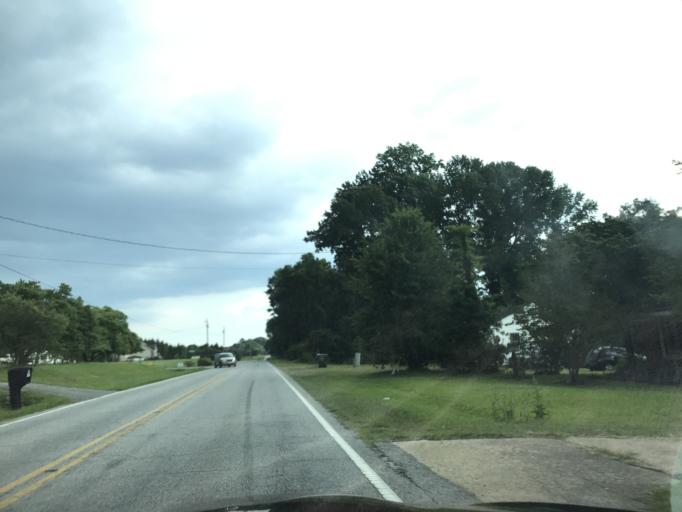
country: US
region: North Carolina
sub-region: Johnston County
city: Four Oaks
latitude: 35.5136
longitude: -78.4883
